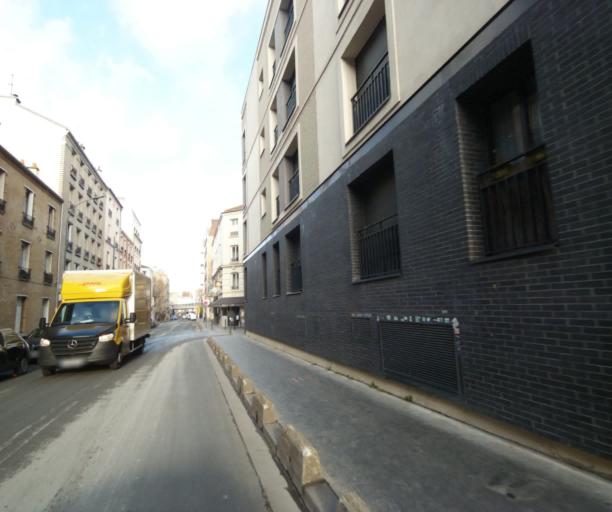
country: FR
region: Ile-de-France
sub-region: Paris
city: Saint-Ouen
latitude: 48.9064
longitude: 2.3357
